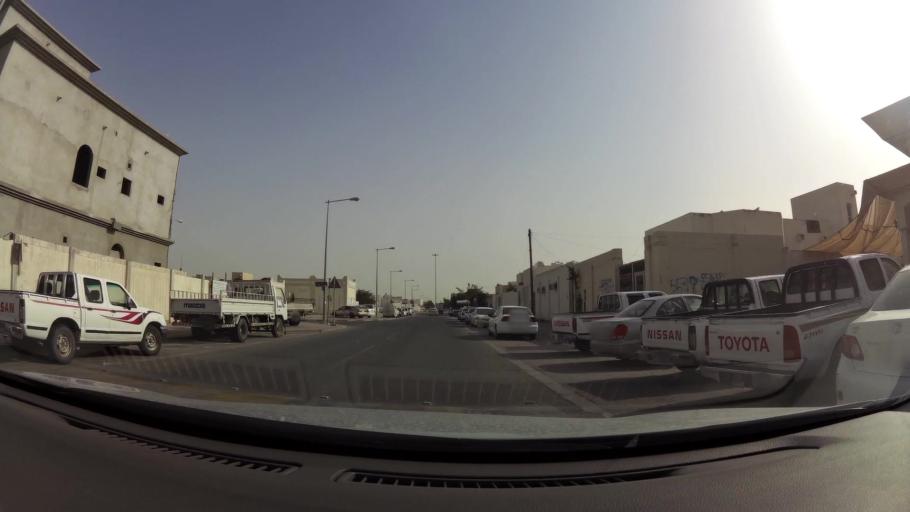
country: QA
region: Baladiyat ar Rayyan
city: Ar Rayyan
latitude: 25.2386
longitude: 51.4367
